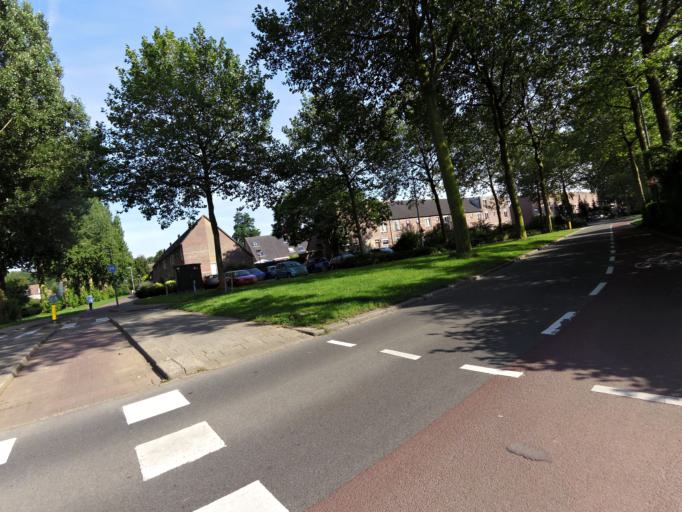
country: NL
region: South Holland
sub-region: Gemeente Sliedrecht
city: Sliedrecht
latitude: 51.7993
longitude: 4.7311
